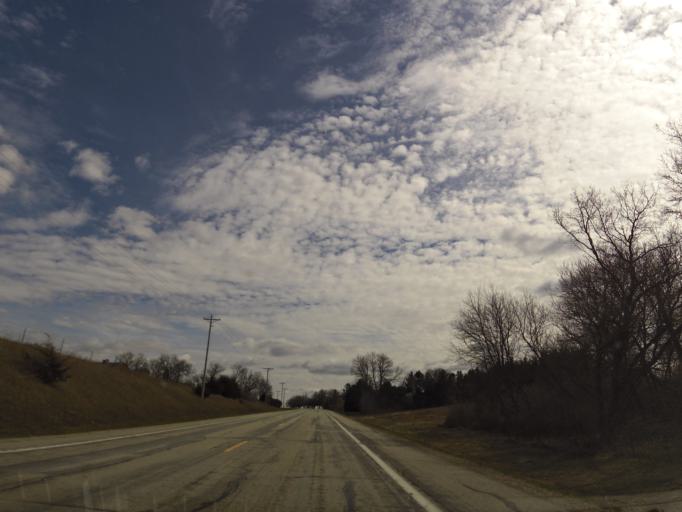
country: US
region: Minnesota
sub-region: Olmsted County
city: Rochester
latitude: 43.9634
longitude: -92.4310
